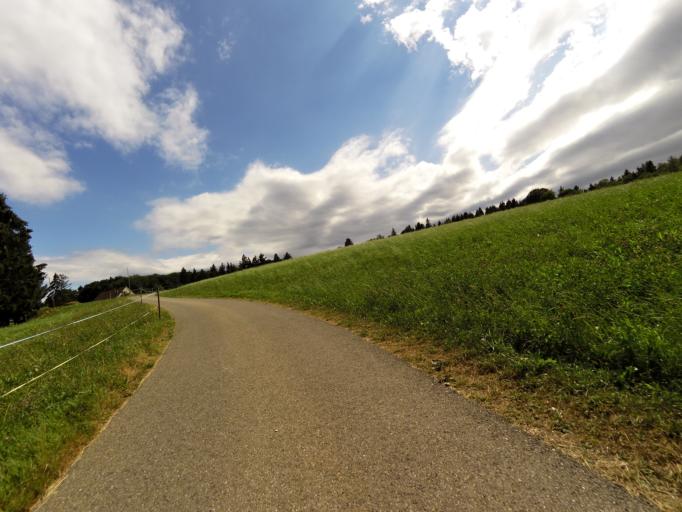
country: CH
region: Thurgau
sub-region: Kreuzlingen District
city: Tagerwilen
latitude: 47.6533
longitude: 9.1097
